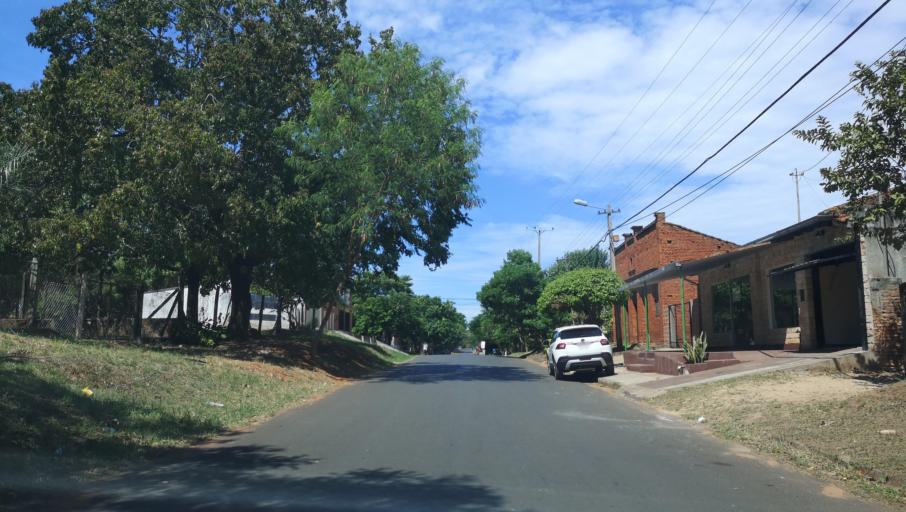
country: PY
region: Misiones
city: Santa Maria
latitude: -26.8899
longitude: -57.0278
